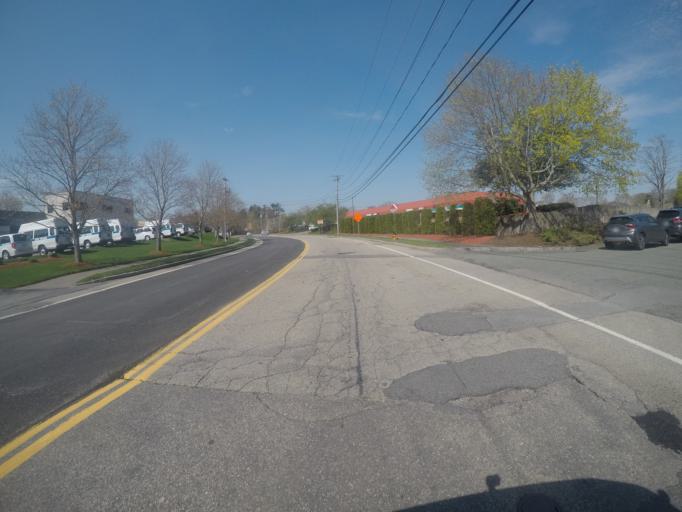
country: US
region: Massachusetts
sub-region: Bristol County
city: Easton
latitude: 42.0473
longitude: -71.0792
